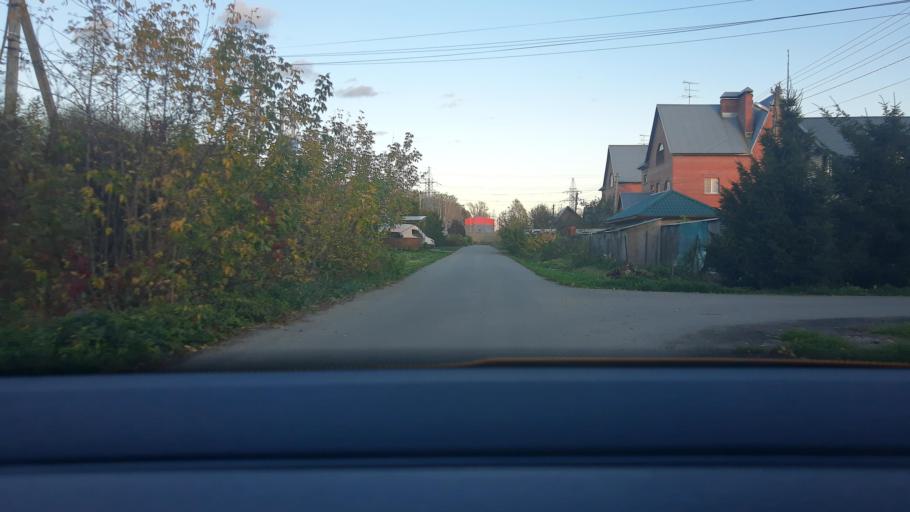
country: RU
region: Moskovskaya
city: Sheremet'yevskiy
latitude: 56.0031
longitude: 37.5272
